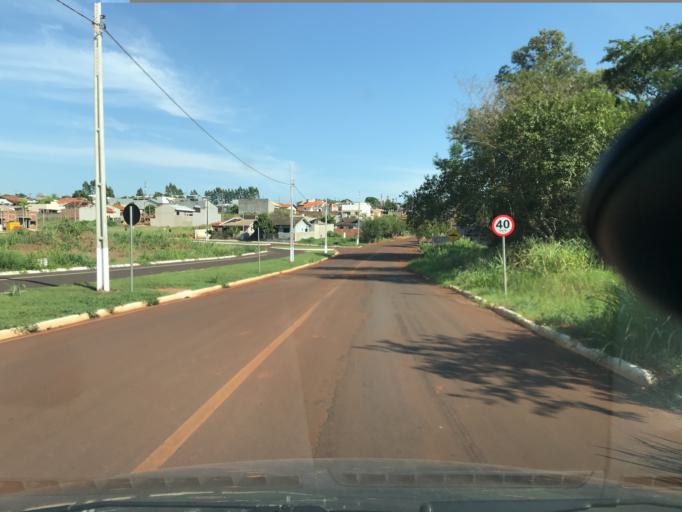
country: BR
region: Parana
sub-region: Palotina
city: Palotina
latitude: -24.2874
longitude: -53.8282
